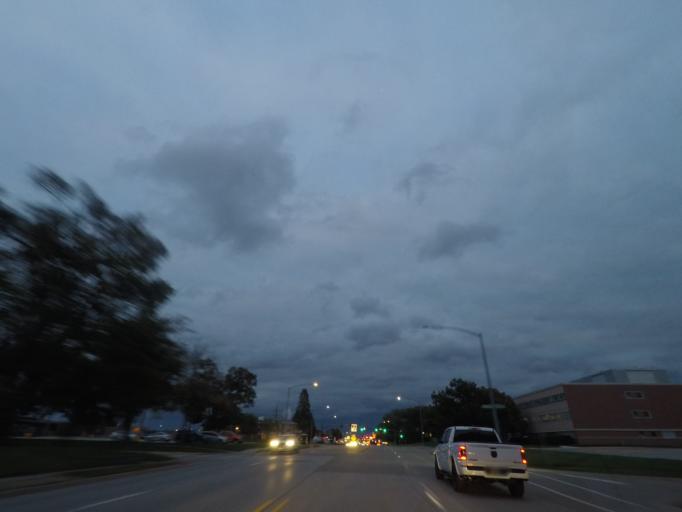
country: US
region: Iowa
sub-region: Story County
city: Ames
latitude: 42.0229
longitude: -93.6241
